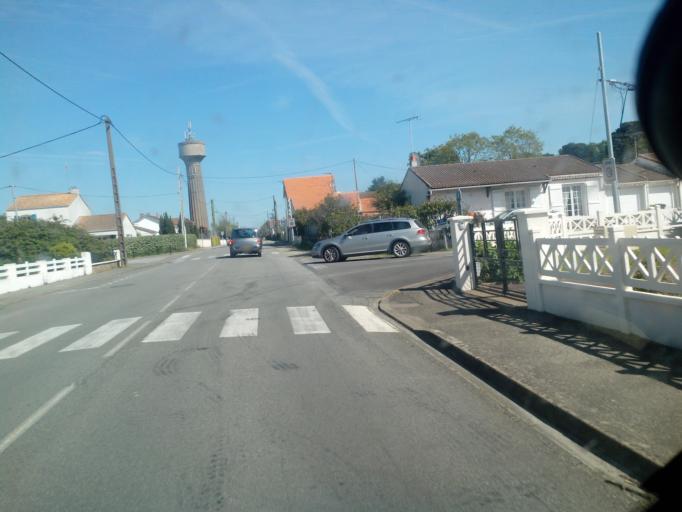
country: FR
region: Pays de la Loire
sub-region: Departement de la Loire-Atlantique
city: Pornic
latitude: 47.1092
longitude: -2.0864
